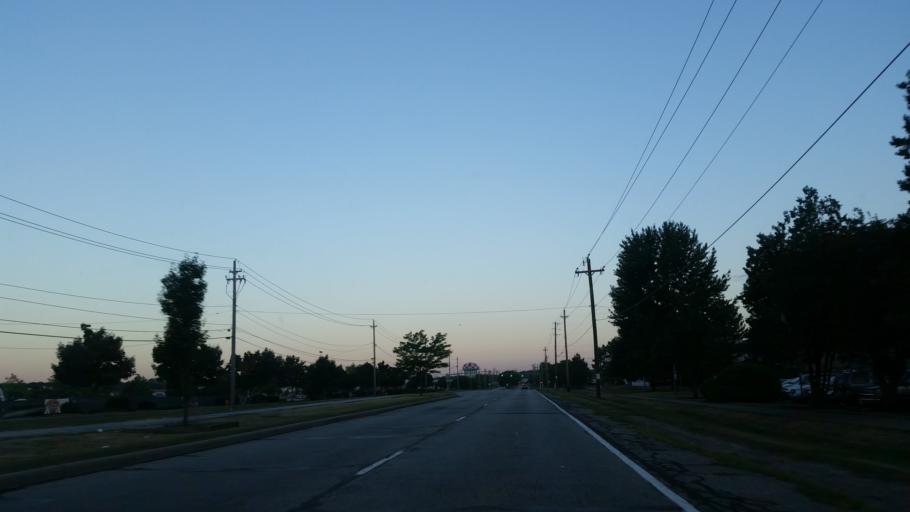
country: US
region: Ohio
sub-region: Cuyahoga County
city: North Olmsted
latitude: 41.4190
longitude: -81.9061
